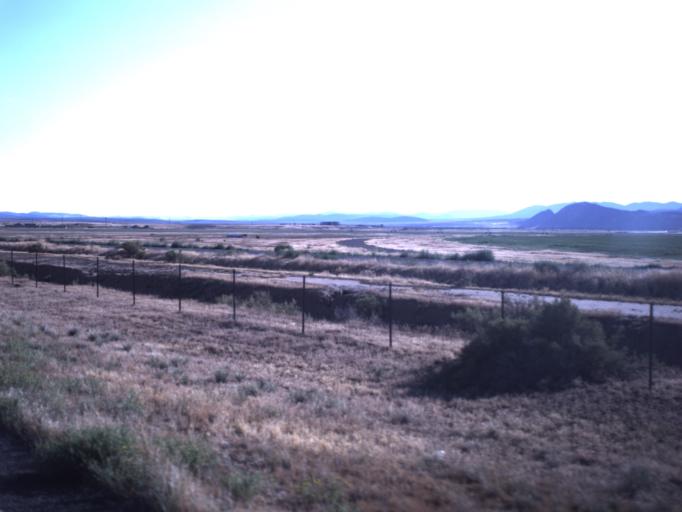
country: US
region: Utah
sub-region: Iron County
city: Enoch
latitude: 37.8798
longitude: -113.0316
